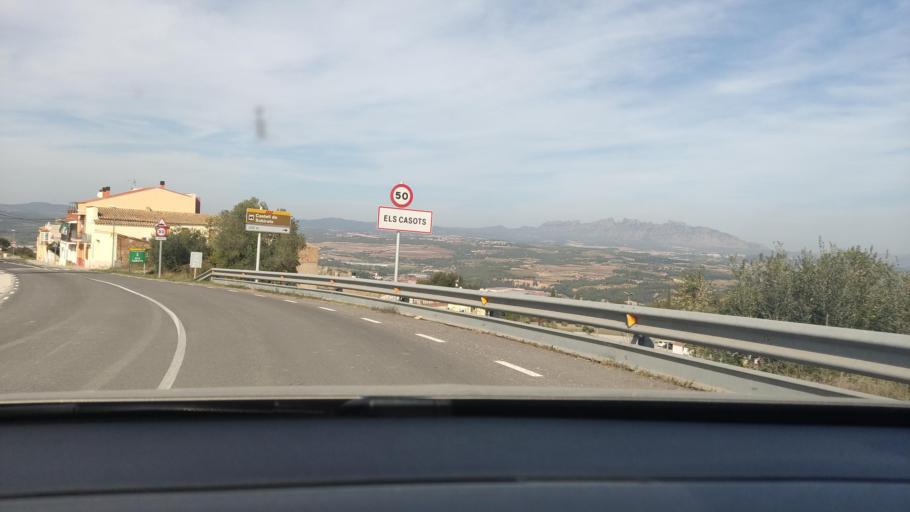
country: ES
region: Catalonia
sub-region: Provincia de Barcelona
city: Subirats
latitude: 41.4071
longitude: 1.8109
